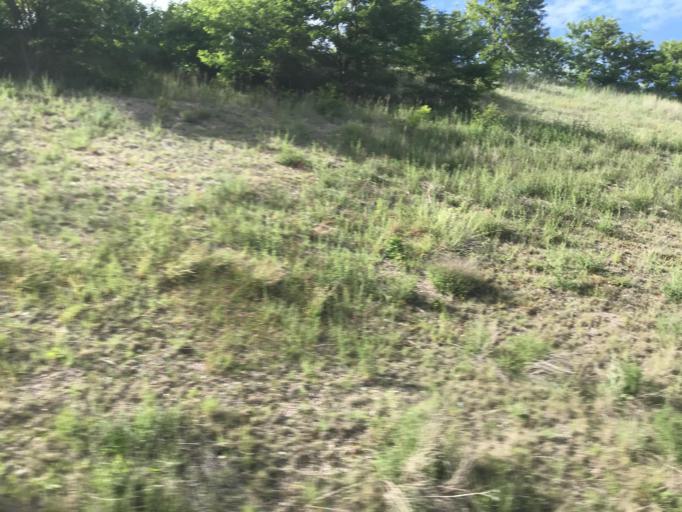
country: DE
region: Thuringia
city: Erfurt
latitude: 50.9809
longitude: 11.0858
